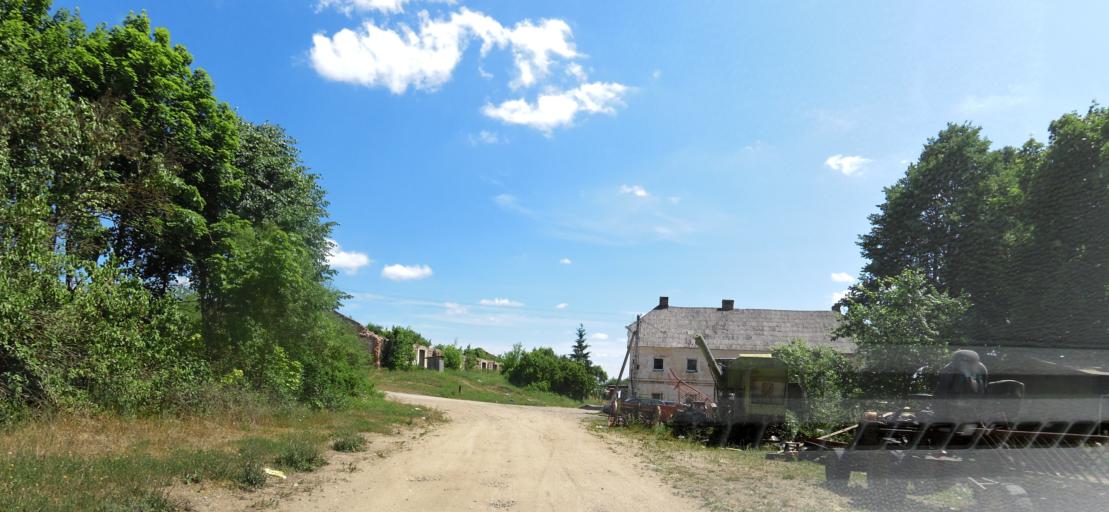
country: LT
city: Nemencine
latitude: 54.8734
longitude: 25.5412
